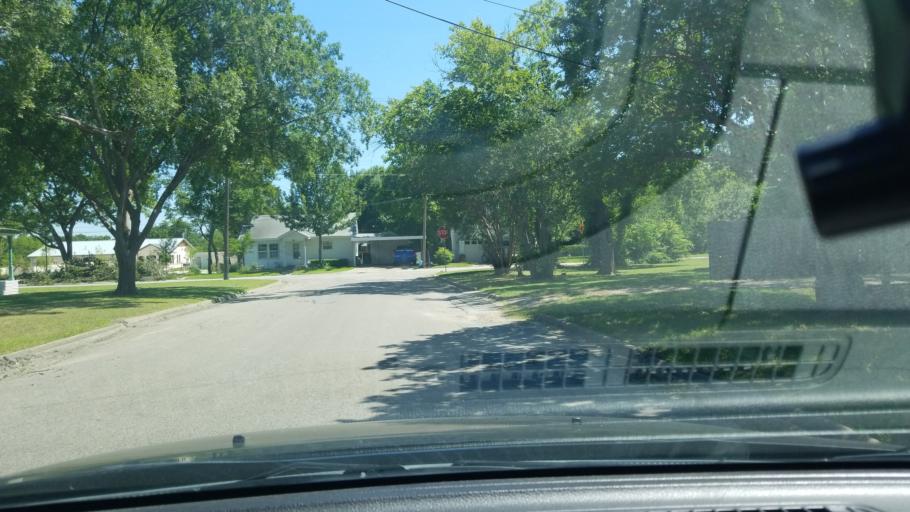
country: US
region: Texas
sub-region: Dallas County
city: Mesquite
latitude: 32.7658
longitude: -96.6017
